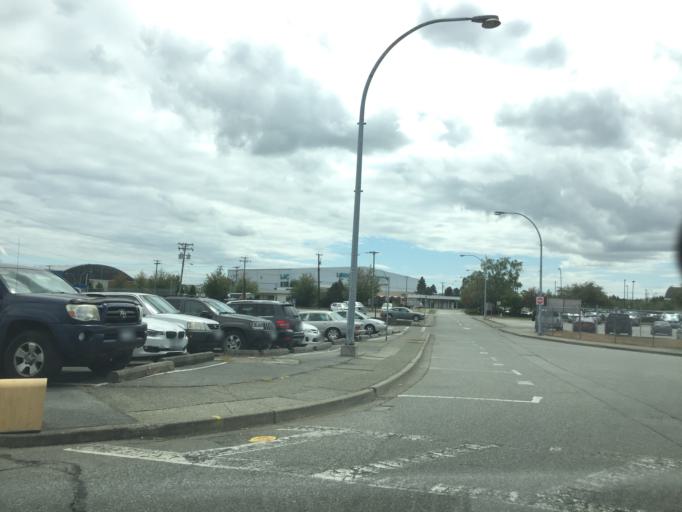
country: CA
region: British Columbia
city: Richmond
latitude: 49.1814
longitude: -123.1691
